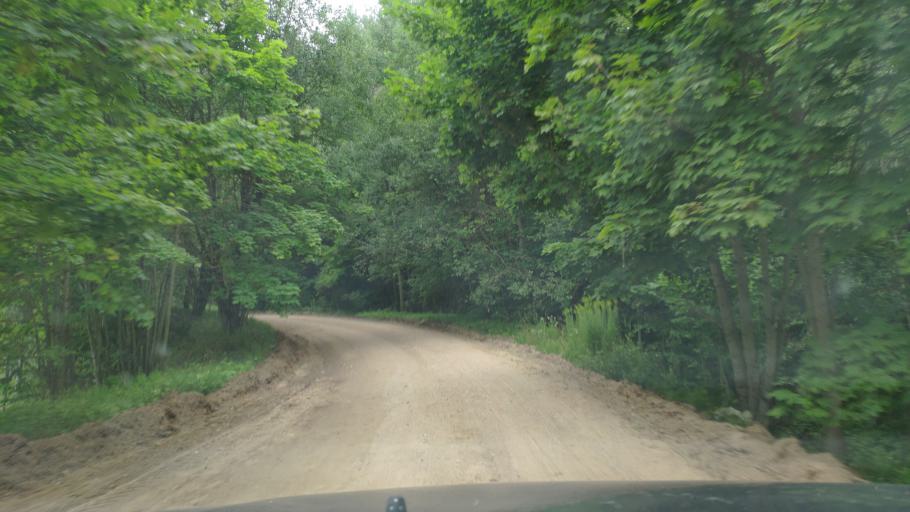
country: BY
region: Minsk
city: Khatsyezhyna
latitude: 53.9351
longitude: 27.2687
